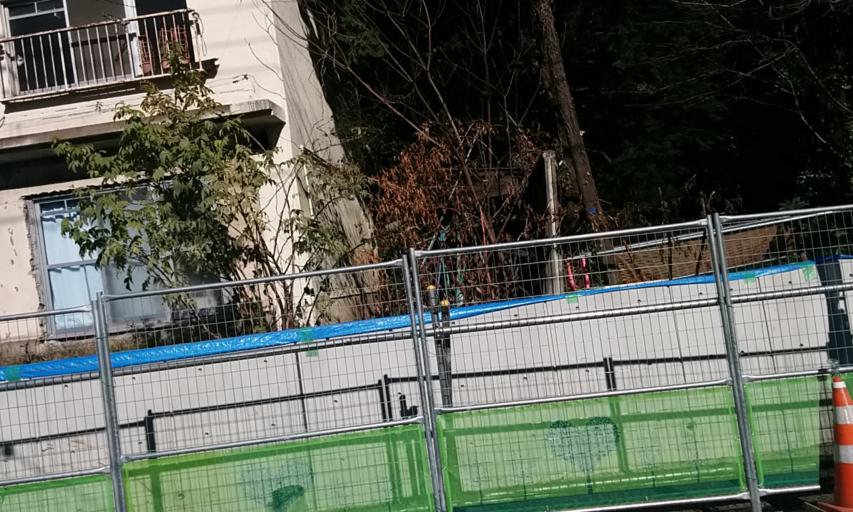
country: JP
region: Tokyo
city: Tokyo
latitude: 35.7183
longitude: 139.7446
